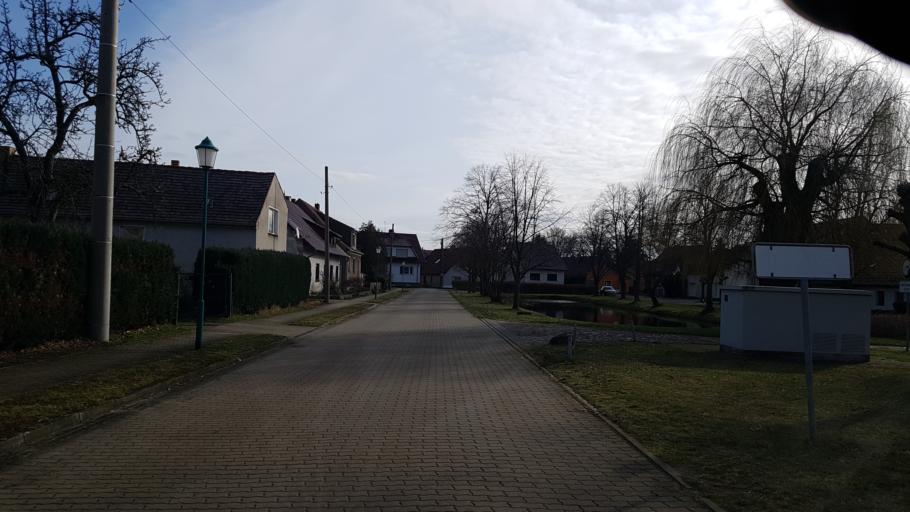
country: DE
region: Brandenburg
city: Schlieben
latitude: 51.7257
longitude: 13.3232
